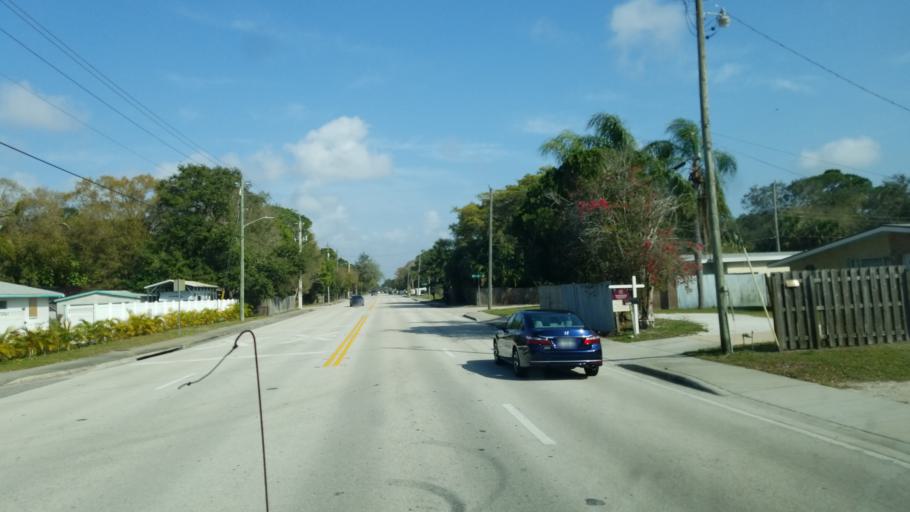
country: US
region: Florida
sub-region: Sarasota County
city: Sarasota Springs
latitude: 27.3083
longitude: -82.4890
